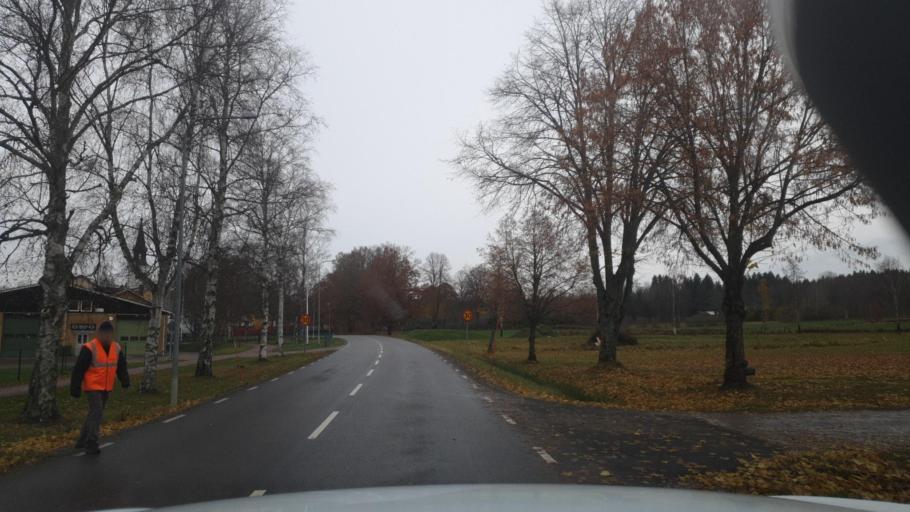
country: SE
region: Vaermland
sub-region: Arvika Kommun
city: Arvika
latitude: 59.5539
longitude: 12.5620
